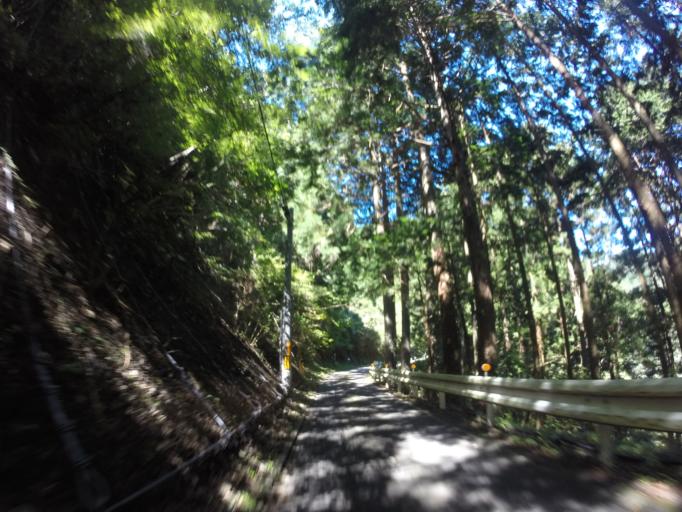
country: JP
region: Shizuoka
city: Fujieda
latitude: 34.9792
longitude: 138.1945
